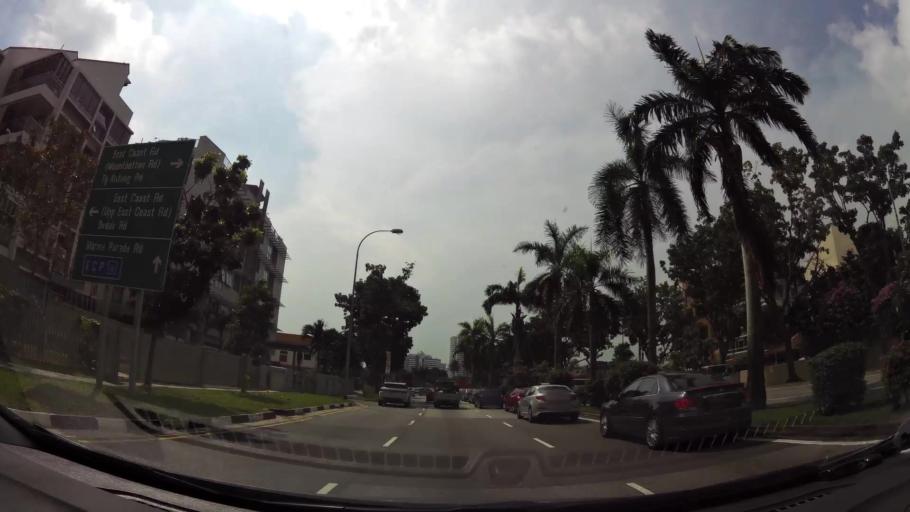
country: SG
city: Singapore
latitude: 1.3098
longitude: 103.9081
